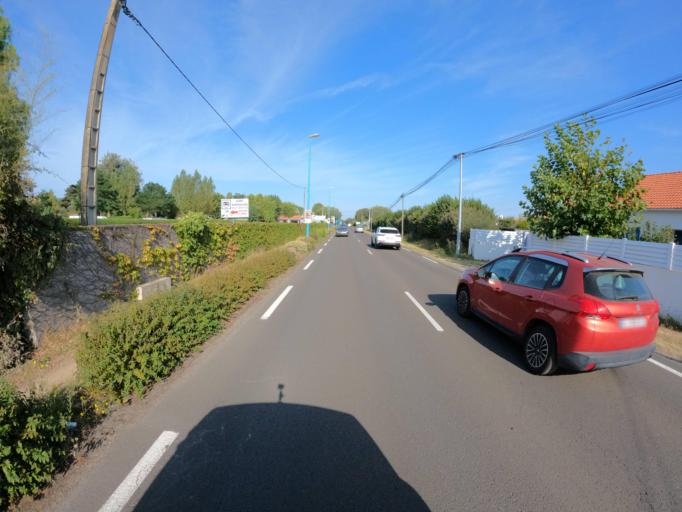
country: FR
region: Pays de la Loire
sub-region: Departement de la Vendee
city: Saint-Jean-de-Monts
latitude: 46.8063
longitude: -2.0985
